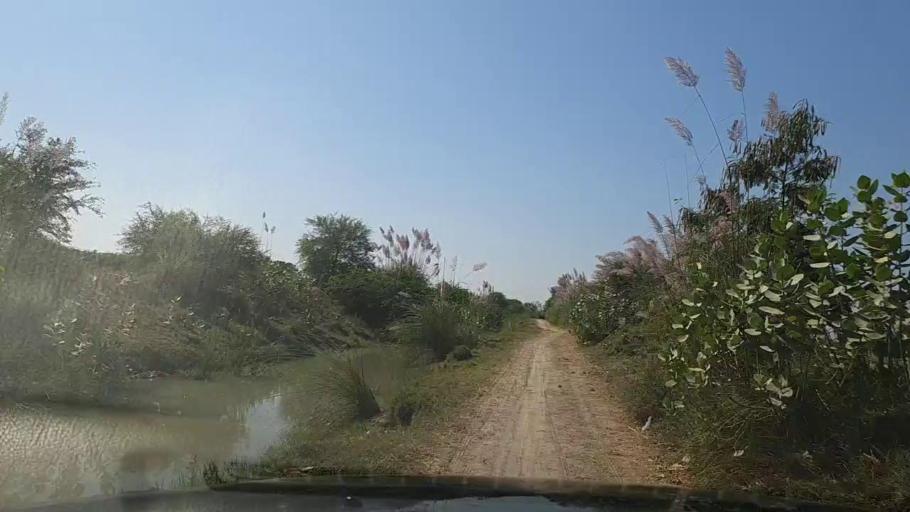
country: PK
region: Sindh
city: Mirpur Sakro
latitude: 24.5815
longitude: 67.8044
